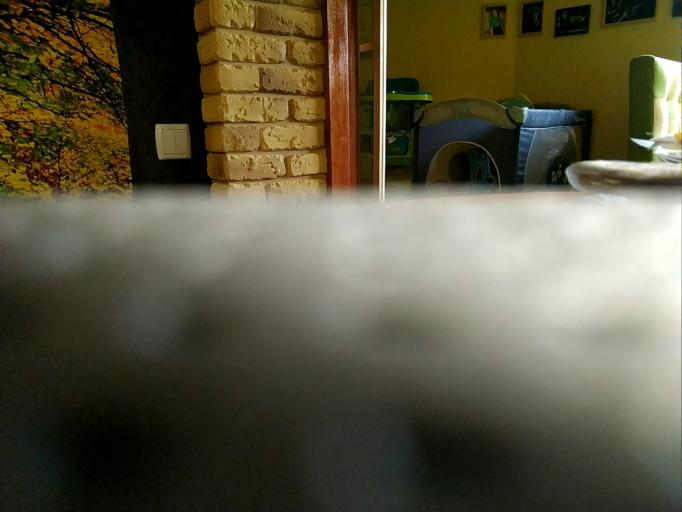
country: RU
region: Kaluga
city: Seredeyskiy
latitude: 53.9093
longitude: 35.3519
